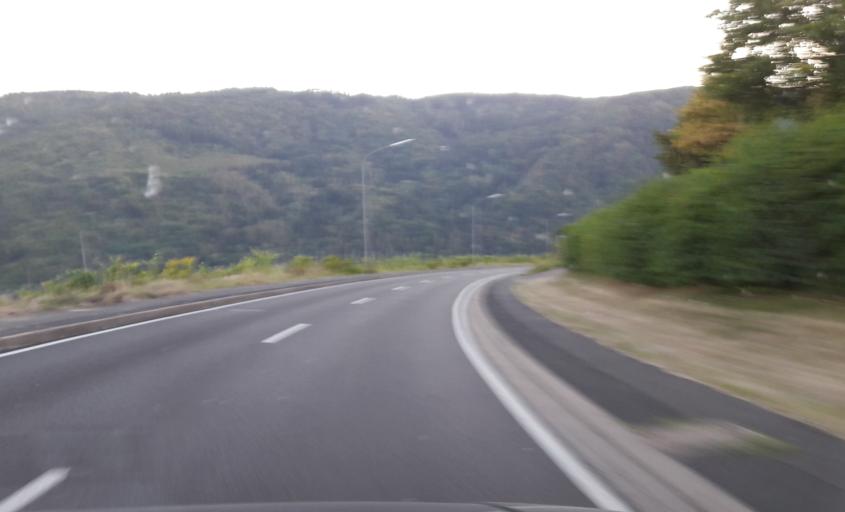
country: DE
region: Rheinland-Pfalz
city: Zell
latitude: 50.0236
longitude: 7.1704
